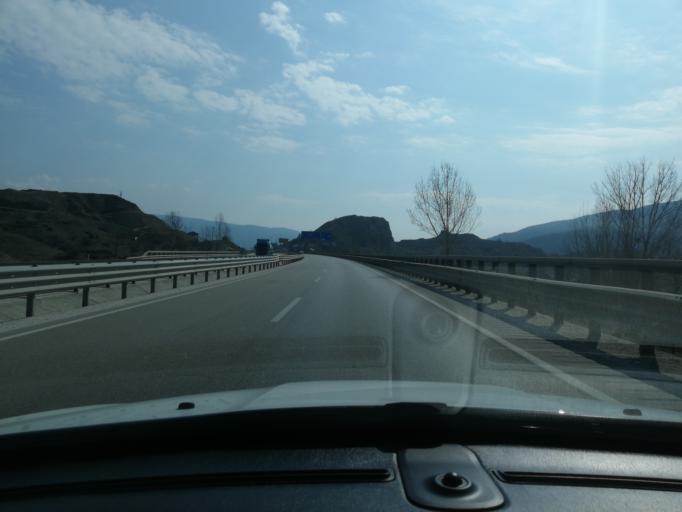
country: TR
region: Cankiri
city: Ilgaz
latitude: 40.9071
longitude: 33.6143
